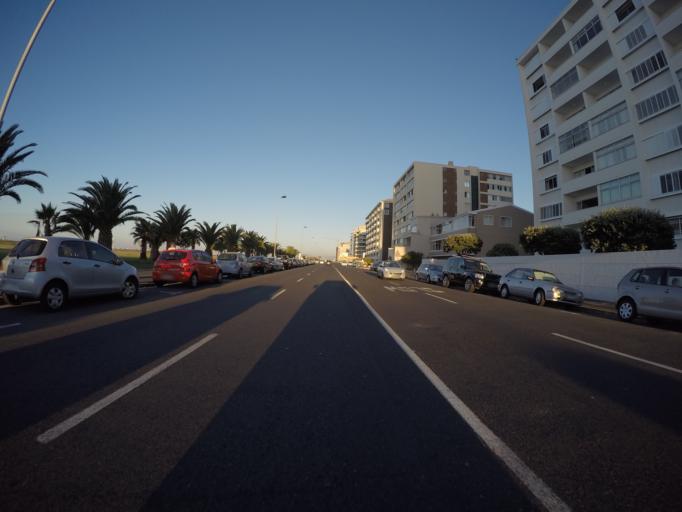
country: ZA
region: Western Cape
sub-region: City of Cape Town
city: Cape Town
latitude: -33.9013
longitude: 18.4009
